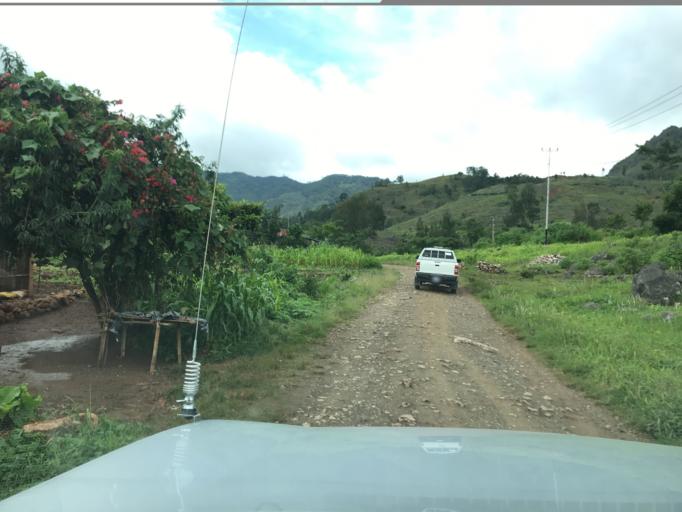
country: TL
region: Aileu
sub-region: Aileu Villa
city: Aileu
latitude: -8.8539
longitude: 125.5799
